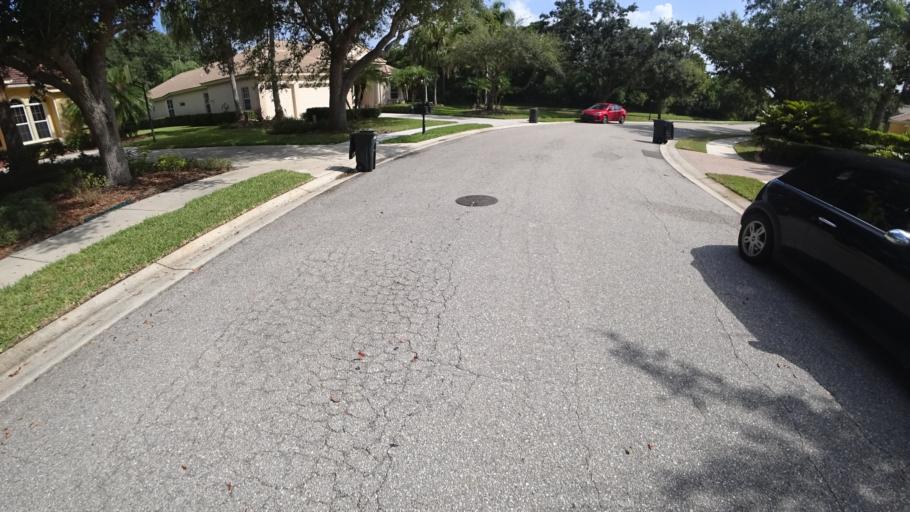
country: US
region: Florida
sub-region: Sarasota County
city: The Meadows
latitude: 27.4008
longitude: -82.4463
